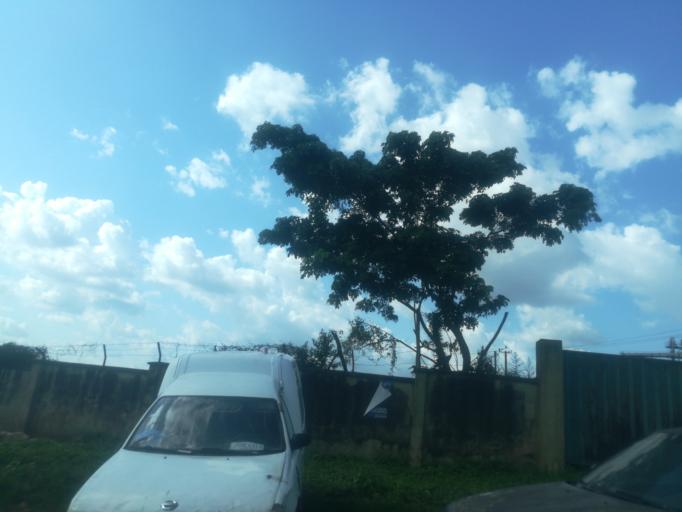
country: NG
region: Oyo
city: Ibadan
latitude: 7.4197
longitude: 3.9684
